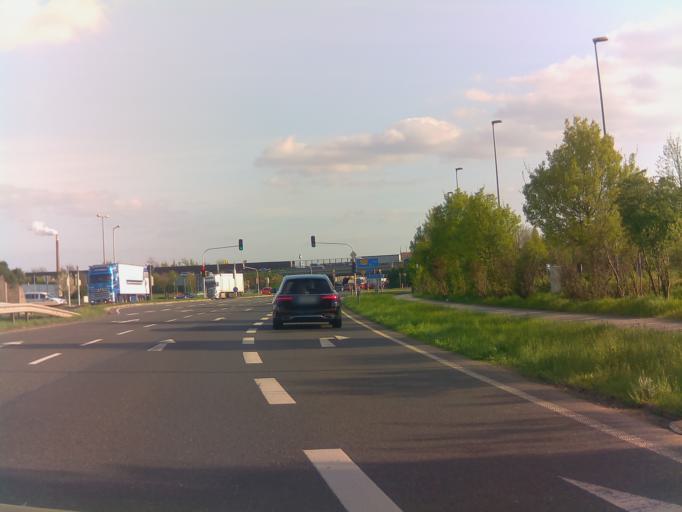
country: DE
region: Hesse
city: Lampertheim
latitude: 49.5567
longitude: 8.4462
